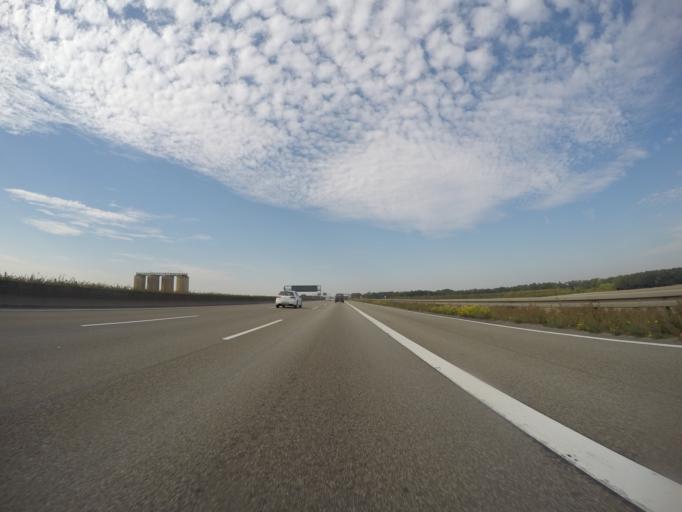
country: DE
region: Hesse
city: Obertshausen
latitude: 50.0601
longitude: 8.8714
